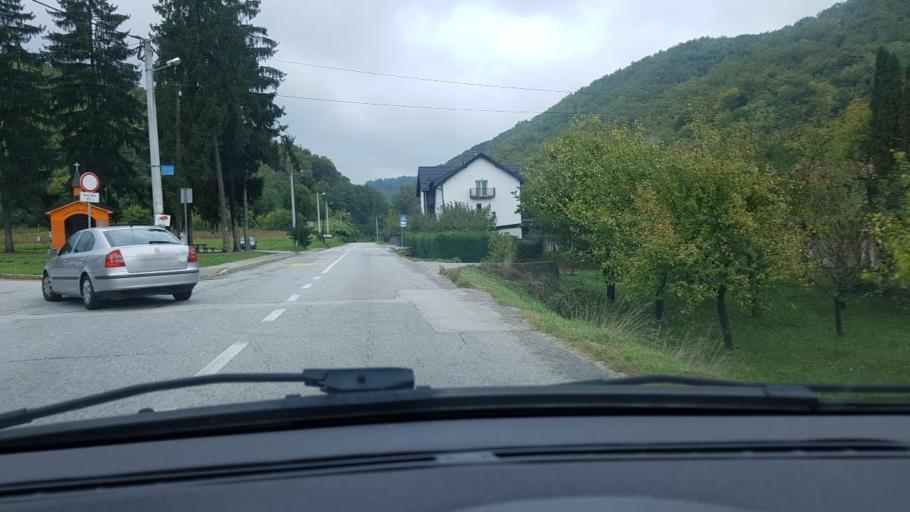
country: HR
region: Krapinsko-Zagorska
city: Marija Bistrica
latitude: 45.9264
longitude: 16.1171
